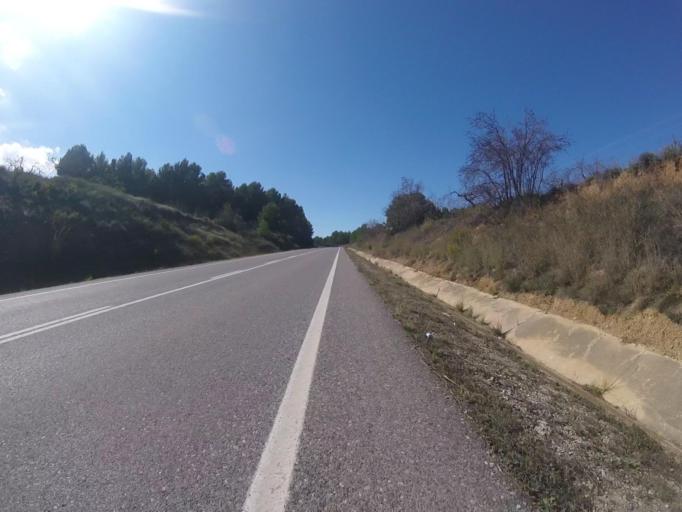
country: ES
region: Valencia
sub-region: Provincia de Castello
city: Sierra-Engarceran
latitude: 40.3208
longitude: -0.0262
